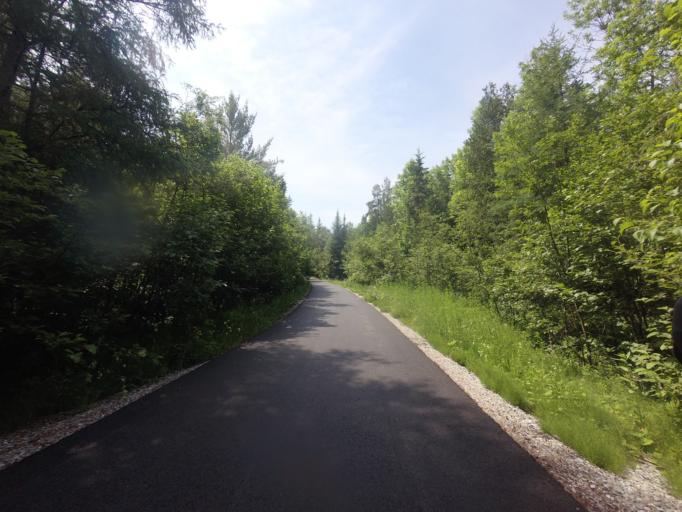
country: CA
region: Quebec
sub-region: Outaouais
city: Maniwaki
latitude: 46.1620
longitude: -76.0484
